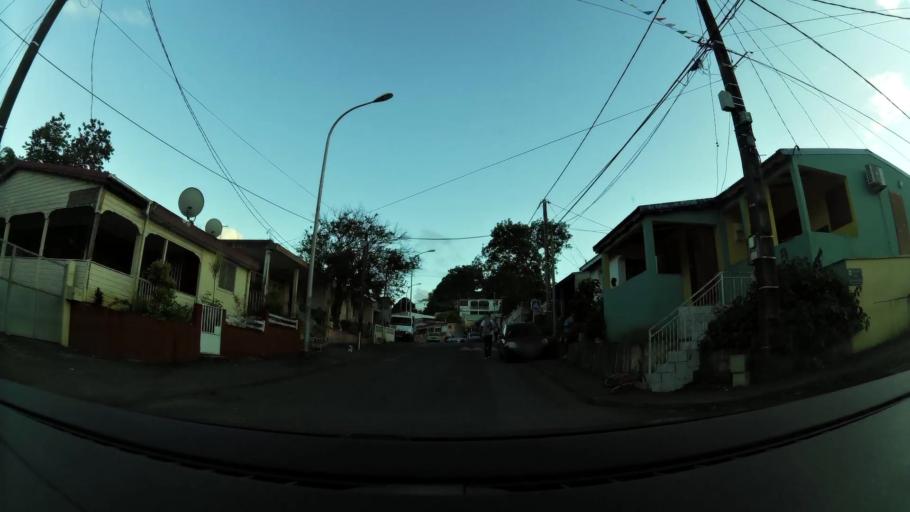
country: GP
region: Guadeloupe
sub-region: Guadeloupe
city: Les Abymes
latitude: 16.2673
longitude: -61.5023
